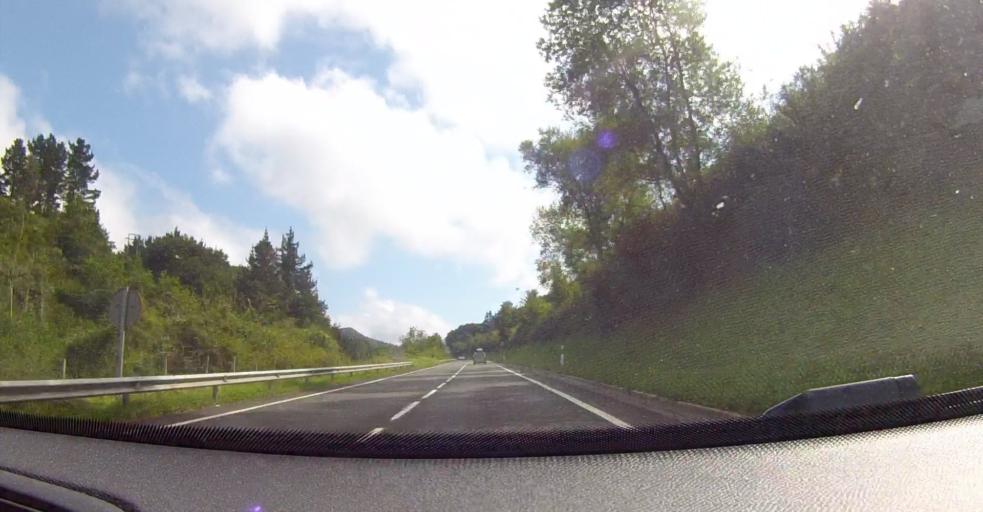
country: ES
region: Basque Country
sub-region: Bizkaia
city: Ibarrangelu
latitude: 43.3730
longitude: -2.6371
